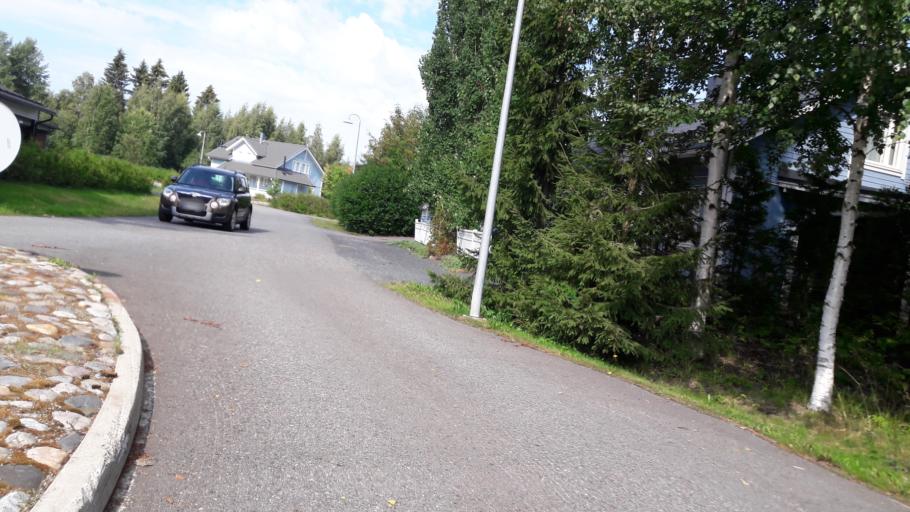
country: FI
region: North Karelia
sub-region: Joensuu
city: Joensuu
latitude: 62.5087
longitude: 29.8262
